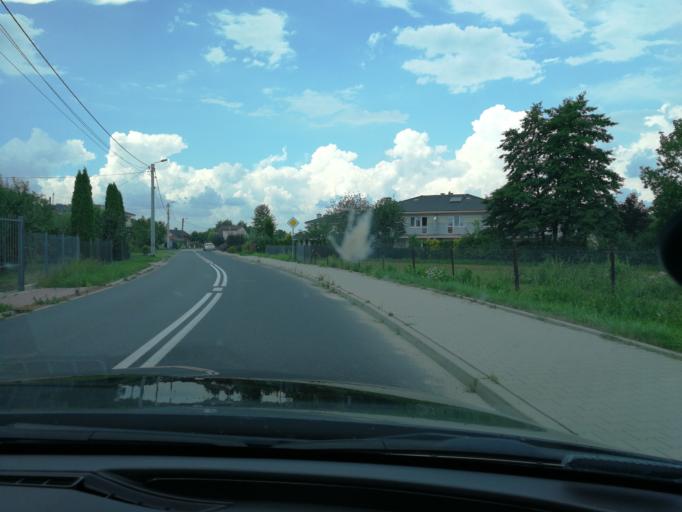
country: PL
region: Lodz Voivodeship
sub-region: Skierniewice
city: Skierniewice
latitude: 51.9735
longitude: 20.1266
